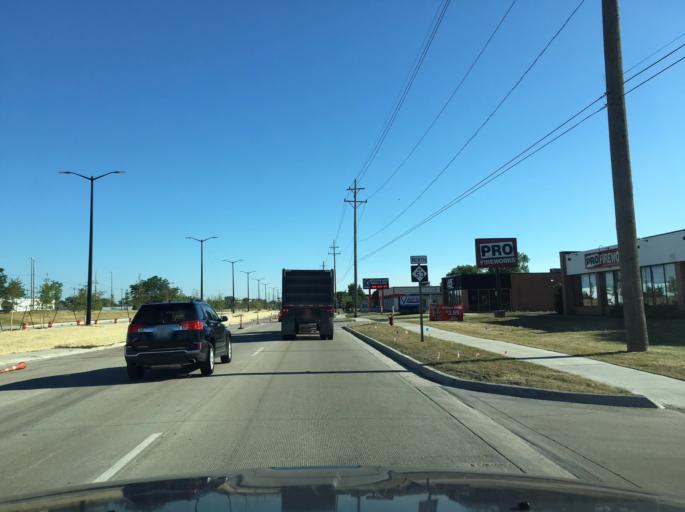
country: US
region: Michigan
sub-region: Macomb County
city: Sterling Heights
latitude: 42.5734
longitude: -83.0298
